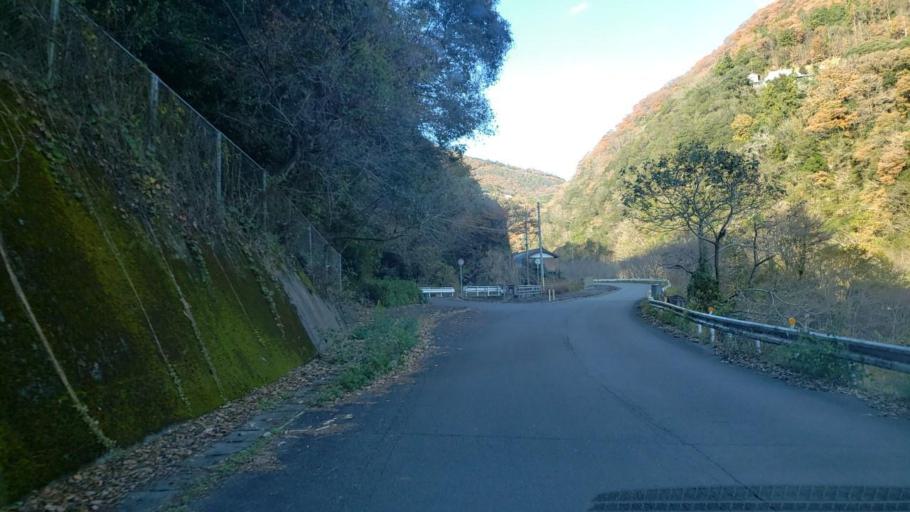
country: JP
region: Tokushima
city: Wakimachi
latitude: 34.0916
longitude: 134.0680
